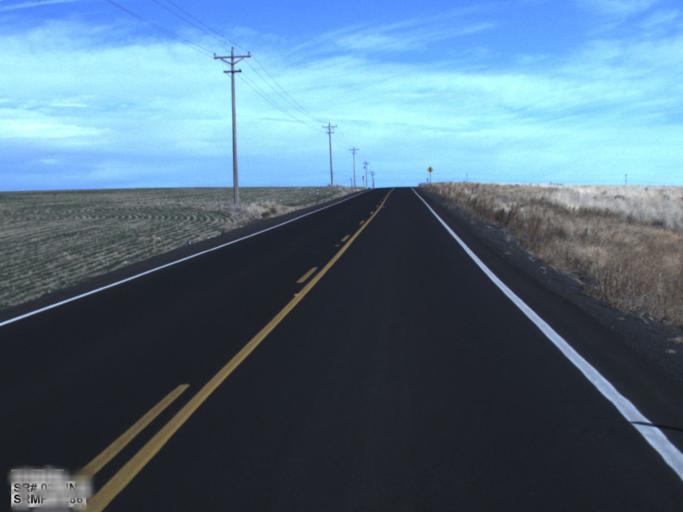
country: US
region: Washington
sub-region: Adams County
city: Ritzville
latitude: 47.1265
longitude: -118.6651
